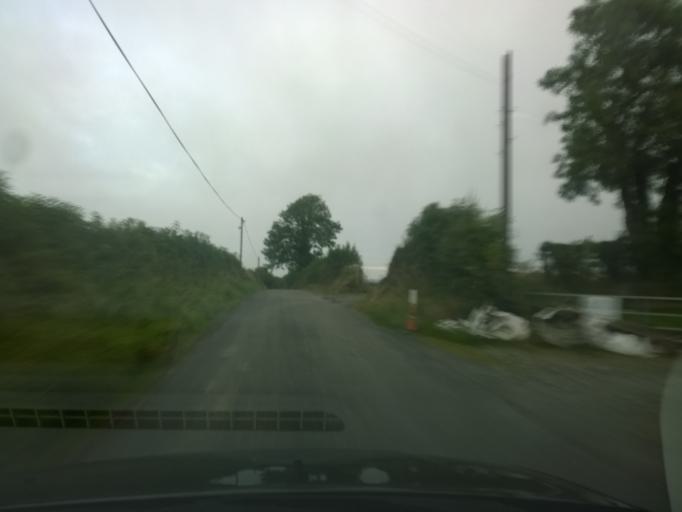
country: IE
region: Leinster
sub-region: Kildare
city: Cherryville
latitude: 53.1832
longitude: -6.9451
